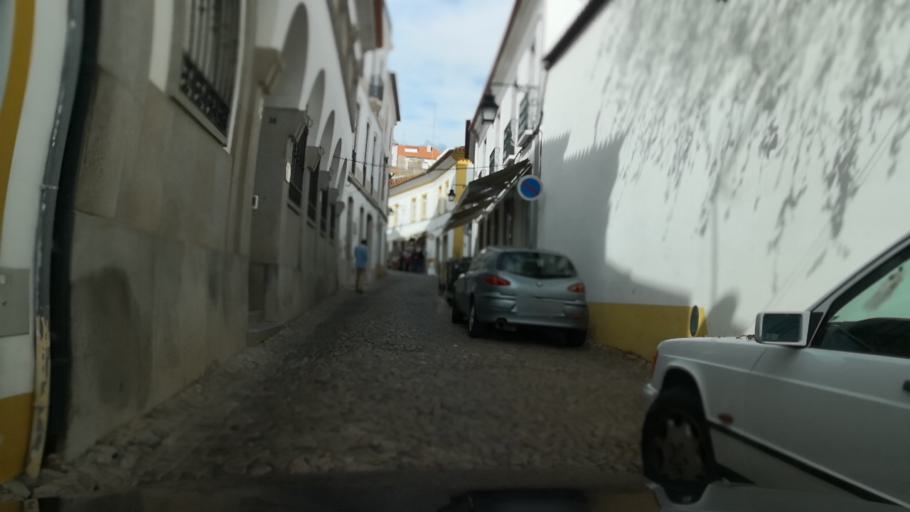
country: PT
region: Evora
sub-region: Evora
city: Evora
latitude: 38.5693
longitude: -7.9098
